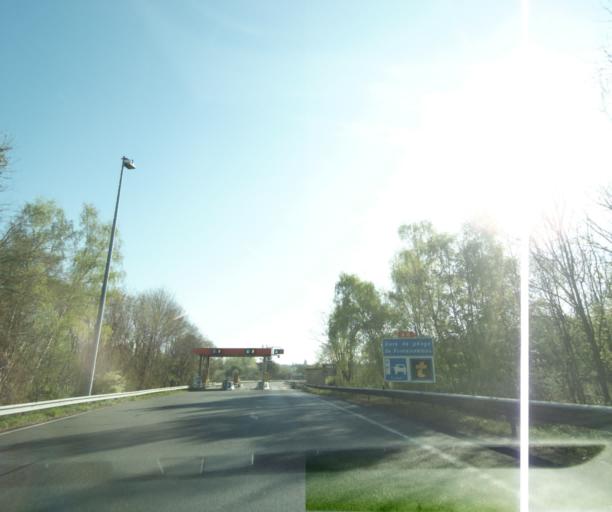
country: FR
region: Ile-de-France
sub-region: Departement de Seine-et-Marne
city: Nemours
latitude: 48.2886
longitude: 2.6824
